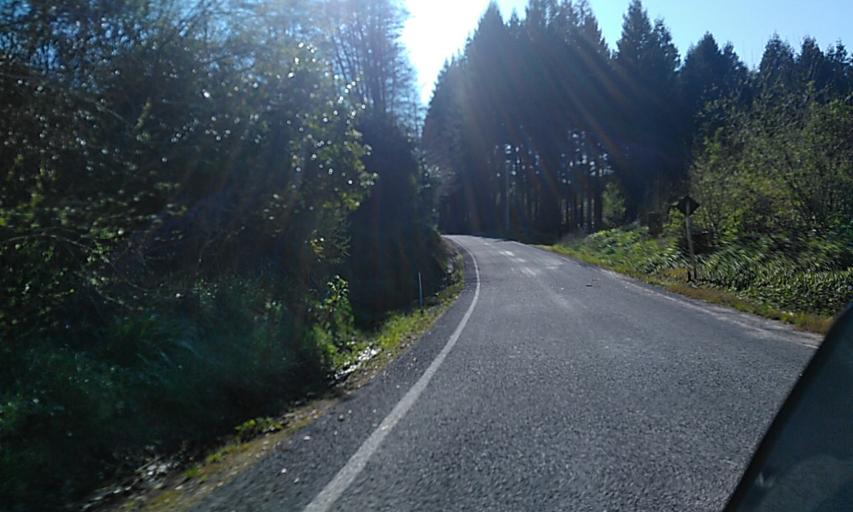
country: NZ
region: Gisborne
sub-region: Gisborne District
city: Gisborne
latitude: -38.5133
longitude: 178.0405
